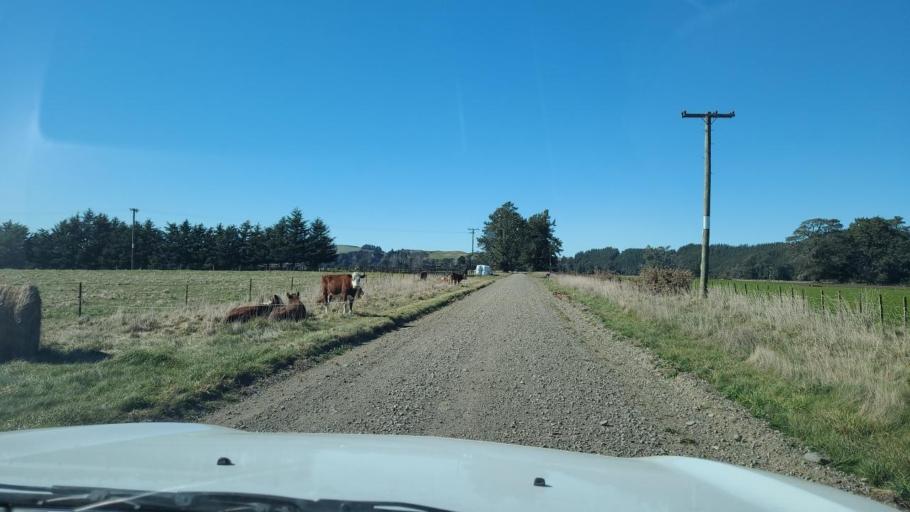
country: NZ
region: Hawke's Bay
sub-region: Napier City
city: Taradale
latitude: -39.4626
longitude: 176.5872
